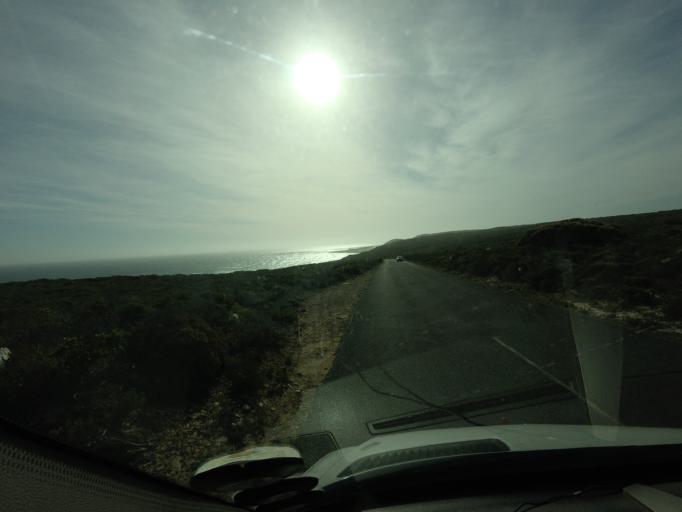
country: ZA
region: Western Cape
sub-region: City of Cape Town
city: Retreat
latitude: -34.3377
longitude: 18.4618
